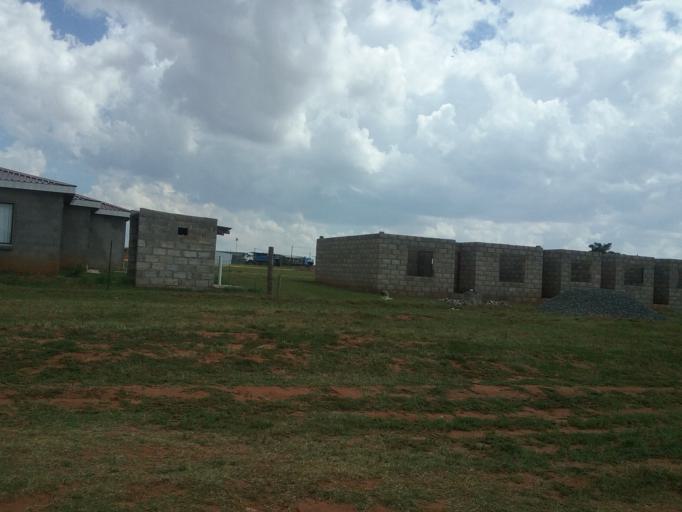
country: LS
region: Maseru
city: Maseru
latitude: -29.4203
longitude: 27.5659
